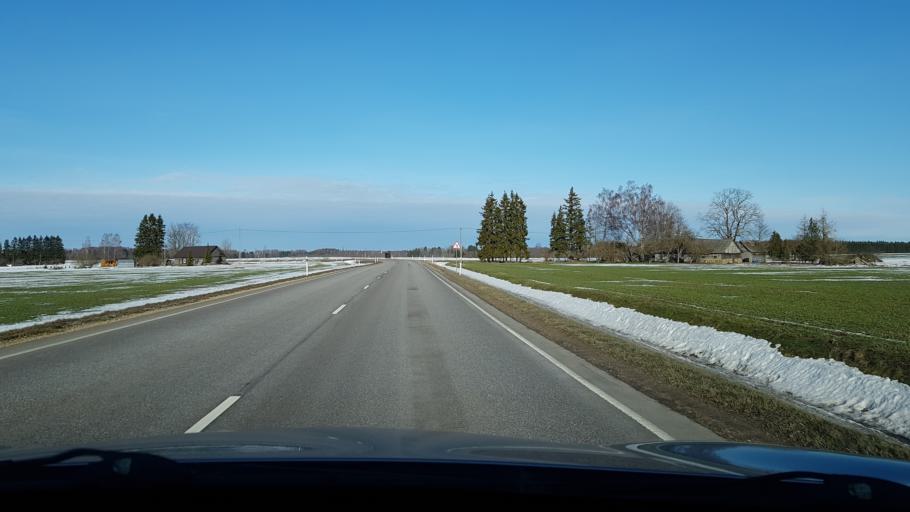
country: EE
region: Jogevamaa
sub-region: Poltsamaa linn
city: Poltsamaa
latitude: 58.6340
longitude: 25.7761
